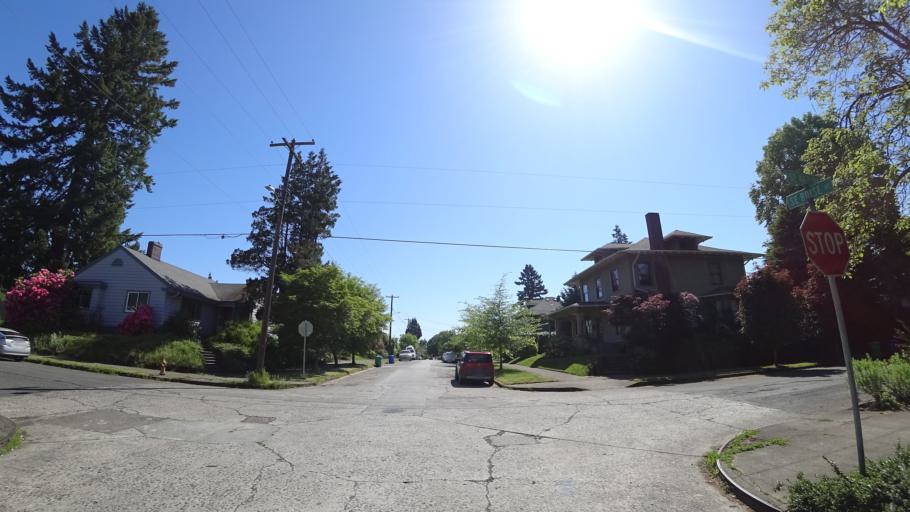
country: US
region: Oregon
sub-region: Multnomah County
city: Lents
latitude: 45.4927
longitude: -122.6151
